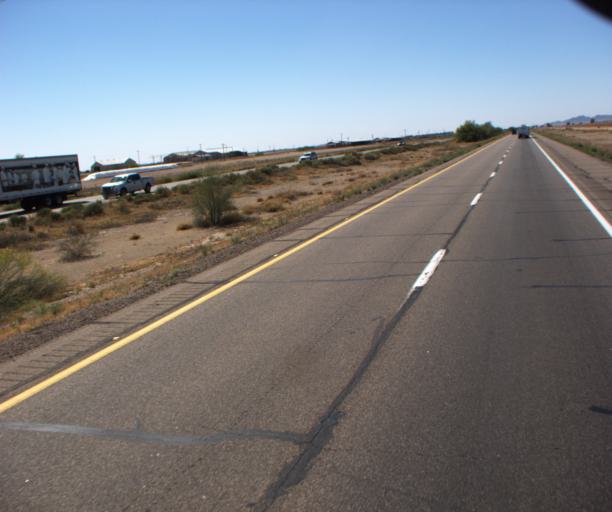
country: US
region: Arizona
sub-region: Maricopa County
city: Gila Bend
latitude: 32.9263
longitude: -112.8555
